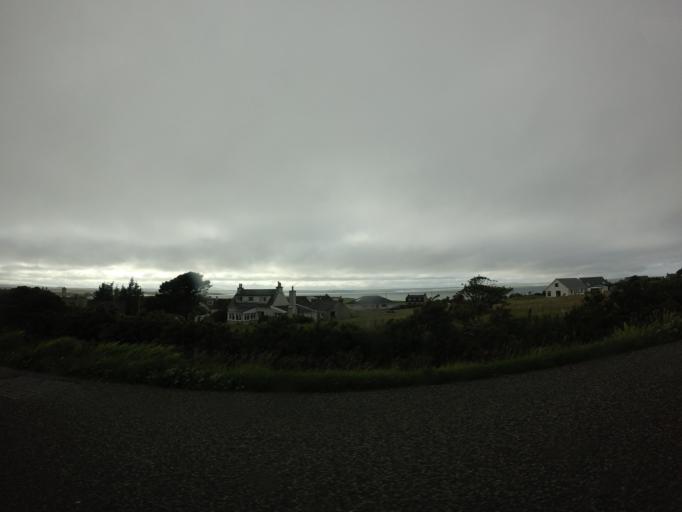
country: GB
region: Scotland
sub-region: Eilean Siar
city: Stornoway
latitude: 58.2067
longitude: -6.2681
